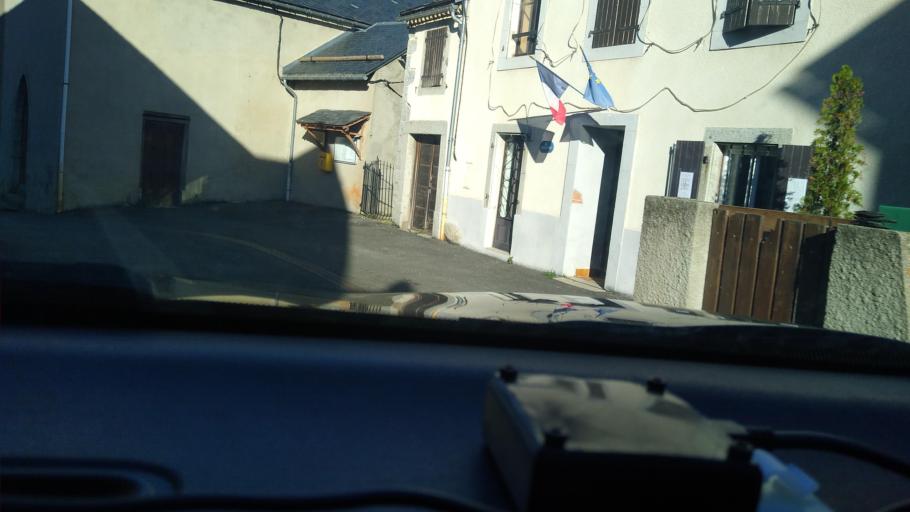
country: FR
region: Languedoc-Roussillon
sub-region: Departement de l'Aude
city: Quillan
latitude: 42.7438
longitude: 2.1640
